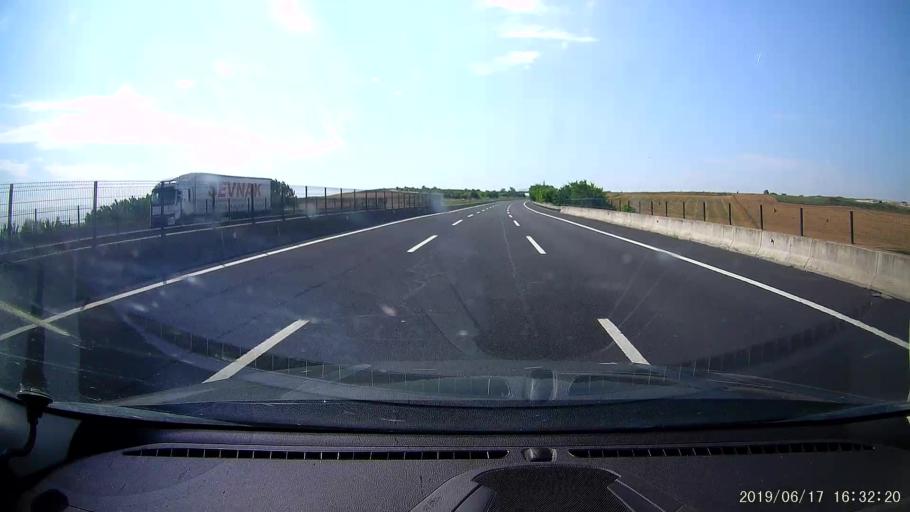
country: TR
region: Kirklareli
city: Buyukkaristiran
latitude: 41.3675
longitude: 27.6021
